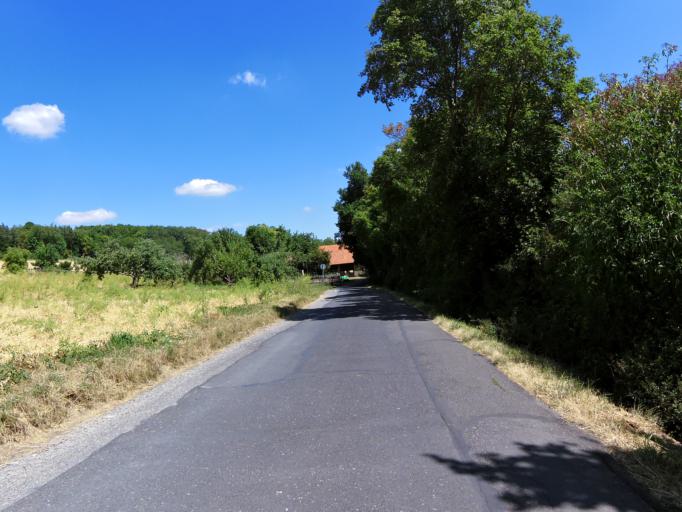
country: DE
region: Bavaria
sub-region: Regierungsbezirk Unterfranken
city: Wuerzburg
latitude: 49.7793
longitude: 9.9203
